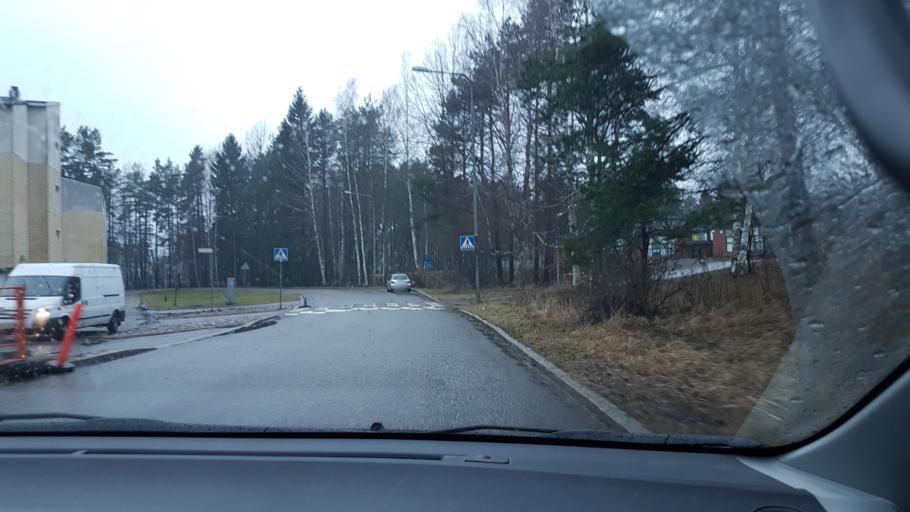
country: FI
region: Uusimaa
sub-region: Helsinki
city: Vantaa
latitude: 60.2334
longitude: 25.0716
